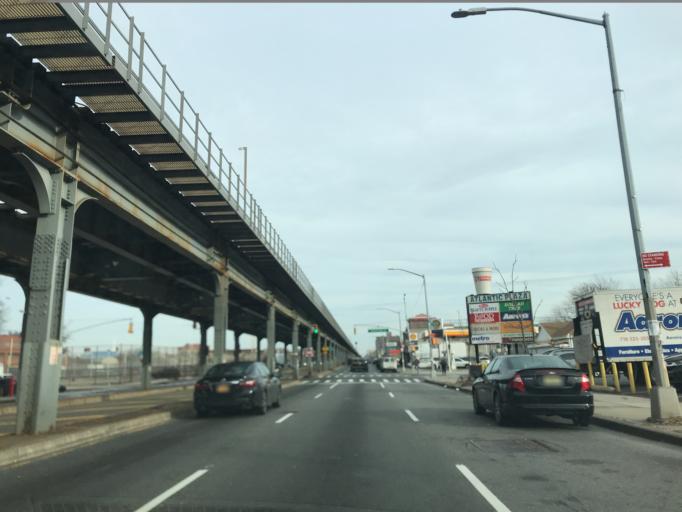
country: US
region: New York
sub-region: Kings County
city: Brooklyn
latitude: 40.6775
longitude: -73.9339
